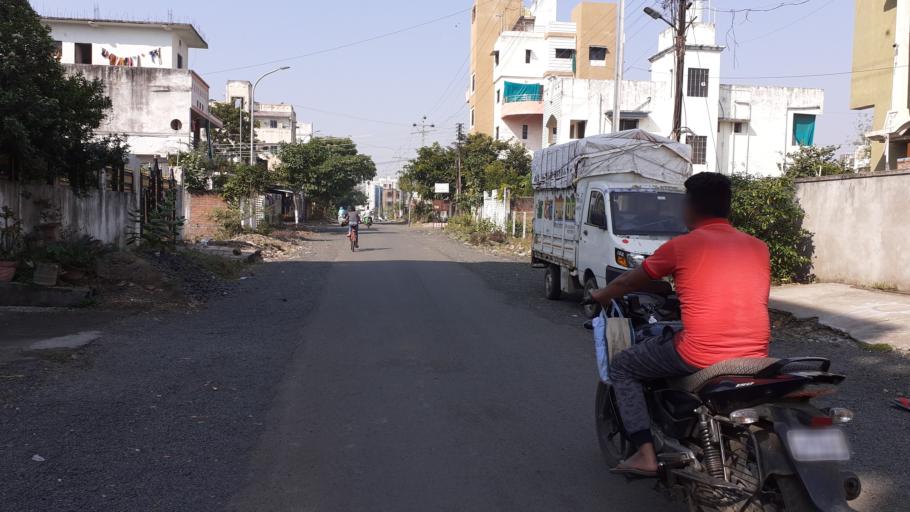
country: IN
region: Maharashtra
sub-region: Nagpur Division
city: Nagpur
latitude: 21.0970
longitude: 79.1108
